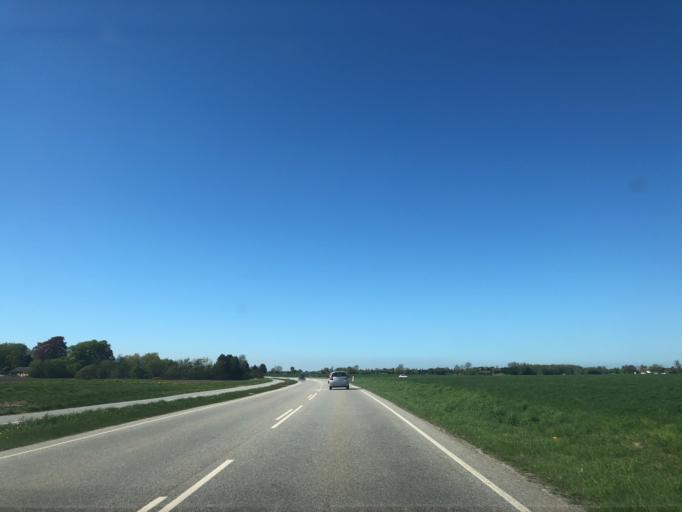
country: DK
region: Zealand
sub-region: Stevns Kommune
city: Store Heddinge
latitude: 55.3477
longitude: 12.3349
